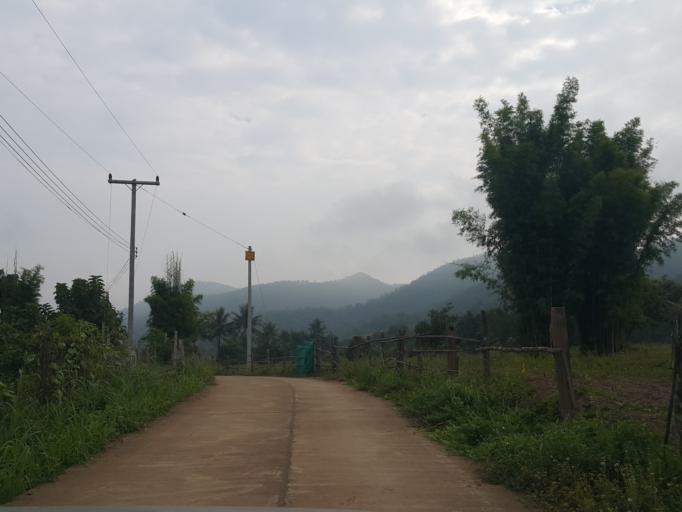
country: TH
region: Mae Hong Son
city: Wiang Nuea
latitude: 19.3766
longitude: 98.4535
